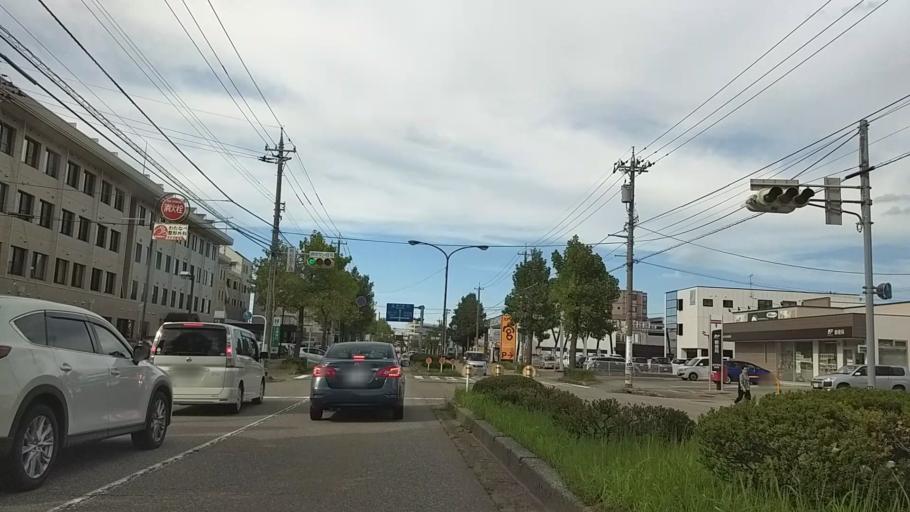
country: JP
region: Ishikawa
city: Nonoichi
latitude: 36.5384
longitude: 136.6394
